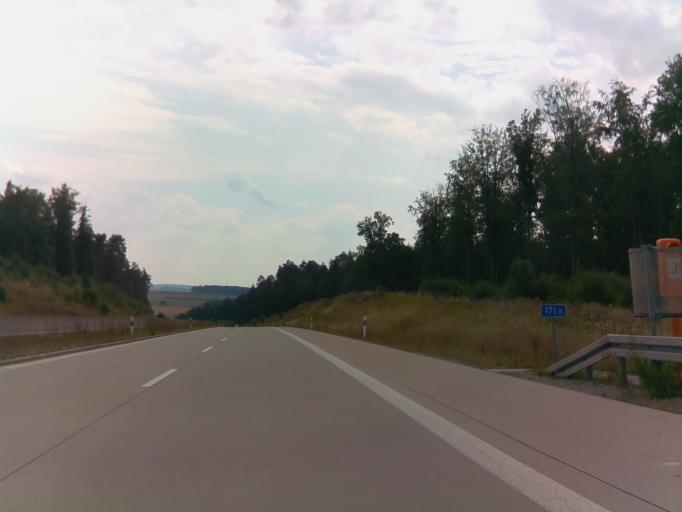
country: DE
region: Bavaria
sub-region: Regierungsbezirk Unterfranken
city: Hendungen
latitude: 50.4014
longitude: 10.3211
